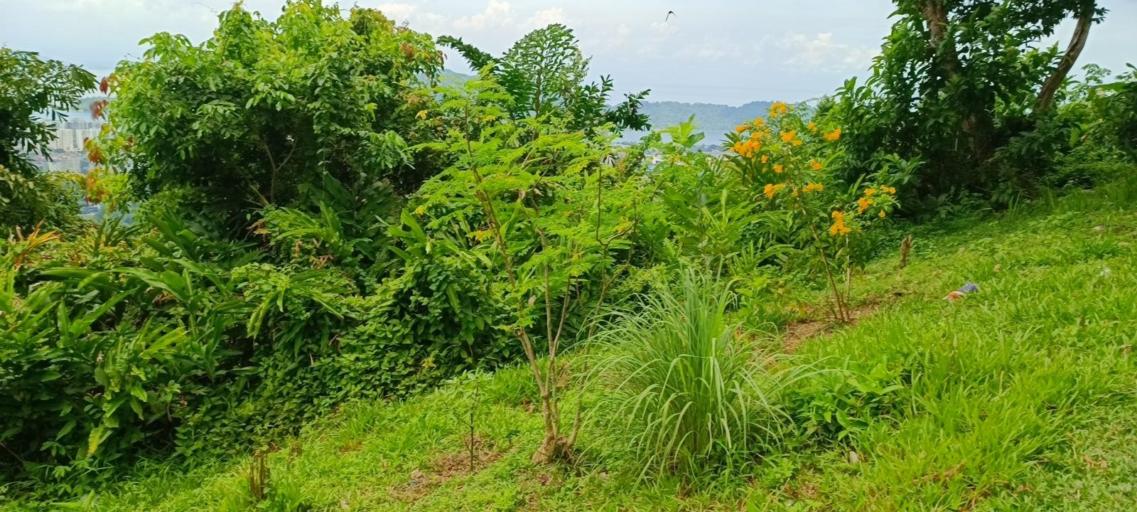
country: MY
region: Penang
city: Kampung Sungai Ara
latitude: 5.3434
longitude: 100.2865
